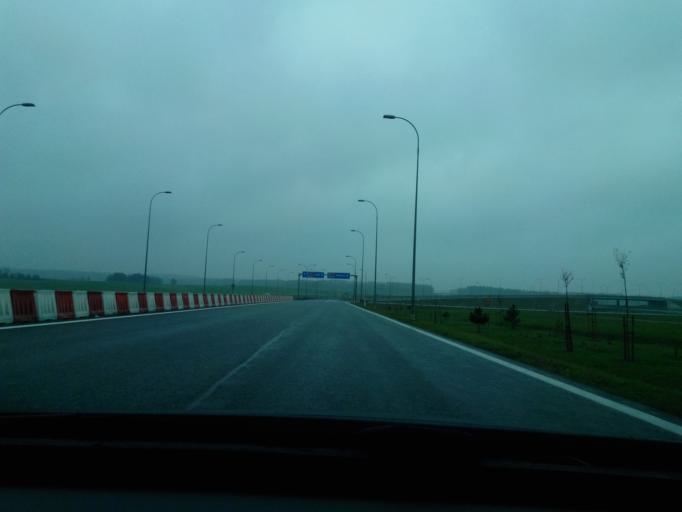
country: PL
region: Pomeranian Voivodeship
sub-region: Powiat tczewski
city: Subkowy
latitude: 54.0342
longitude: 18.6742
